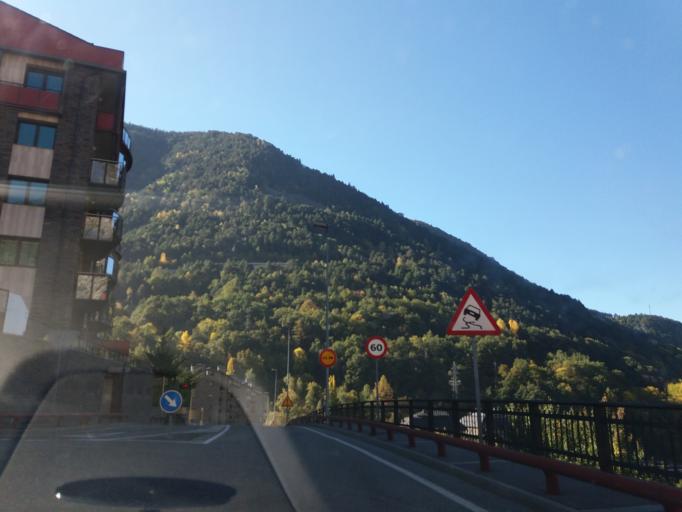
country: AD
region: Escaldes-Engordany
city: les Escaldes
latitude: 42.5100
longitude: 1.5481
